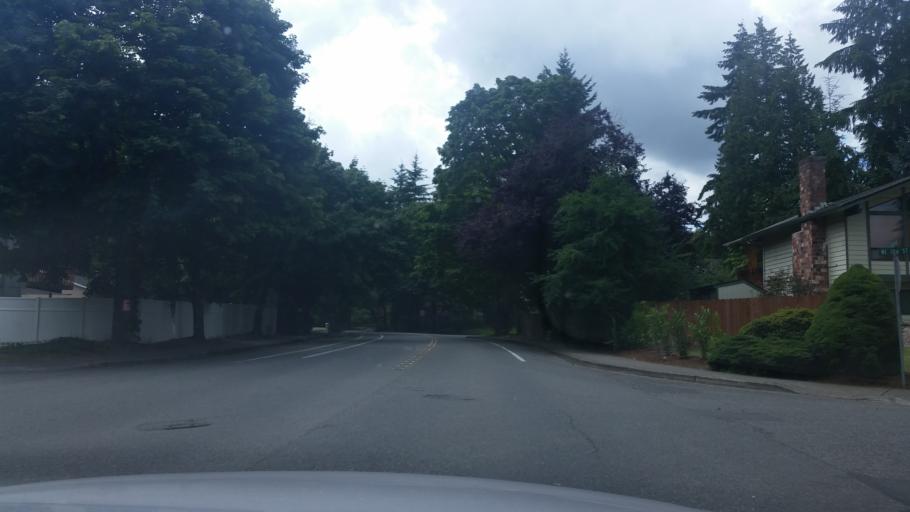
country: US
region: Washington
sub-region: King County
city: Redmond
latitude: 47.6953
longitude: -122.1266
